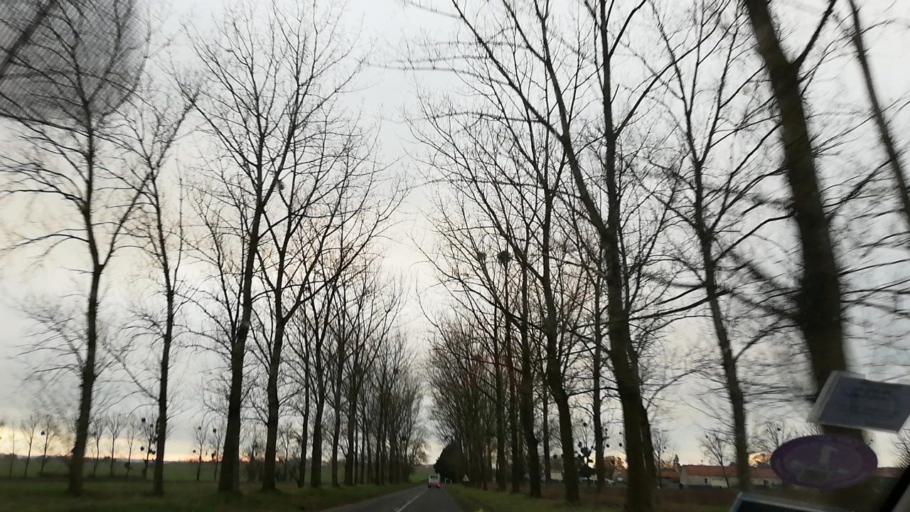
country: FR
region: Ile-de-France
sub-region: Departement de Seine-et-Marne
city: Charny
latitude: 48.9807
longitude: 2.7899
